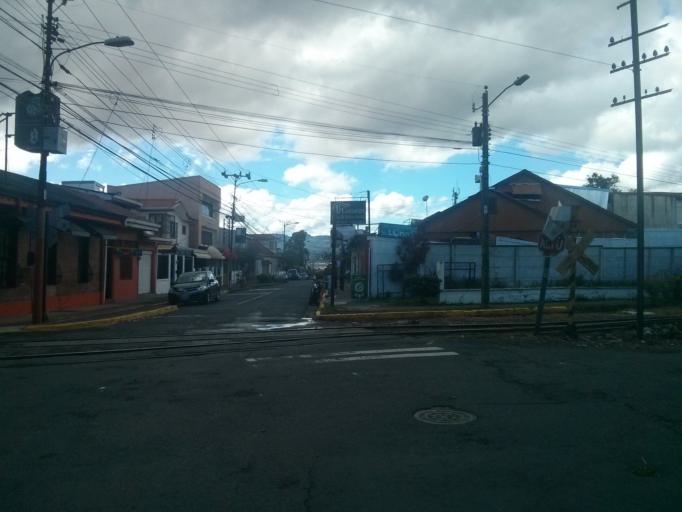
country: CR
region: San Jose
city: San Pedro
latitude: 9.9340
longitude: -84.0635
